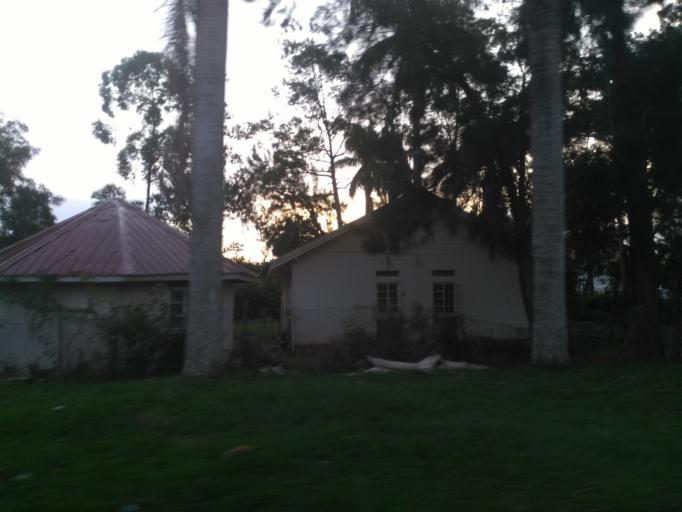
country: UG
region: Eastern Region
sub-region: Jinja District
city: Jinja
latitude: 0.4298
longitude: 33.2016
